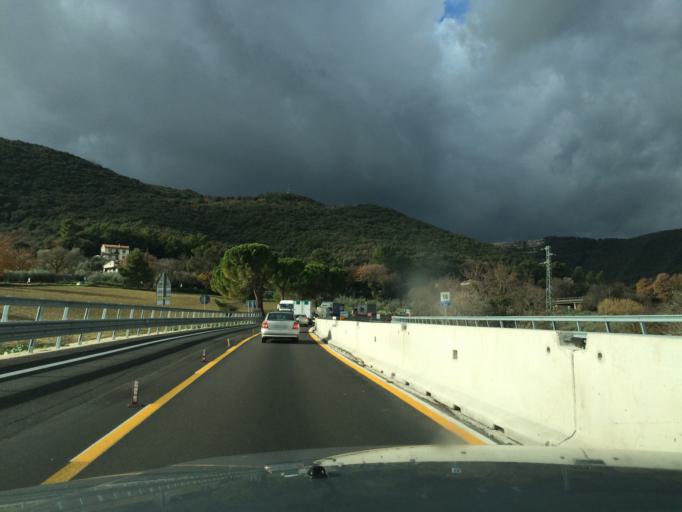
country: IT
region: Umbria
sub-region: Provincia di Terni
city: Narni Scalo
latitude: 42.5397
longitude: 12.5050
